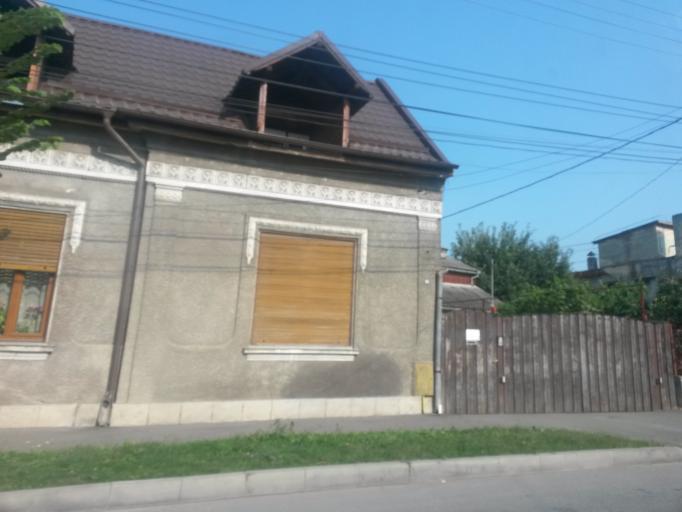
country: RO
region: Cluj
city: Turda
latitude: 46.5728
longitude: 23.7797
